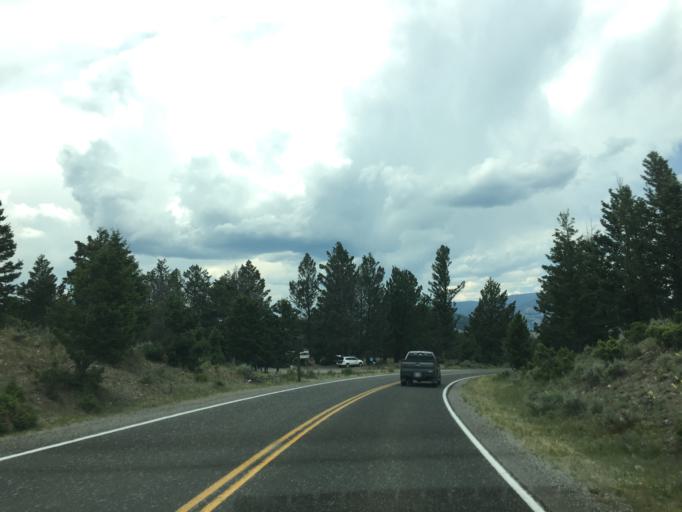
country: US
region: Montana
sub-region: Gallatin County
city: West Yellowstone
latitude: 44.9165
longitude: -110.3992
